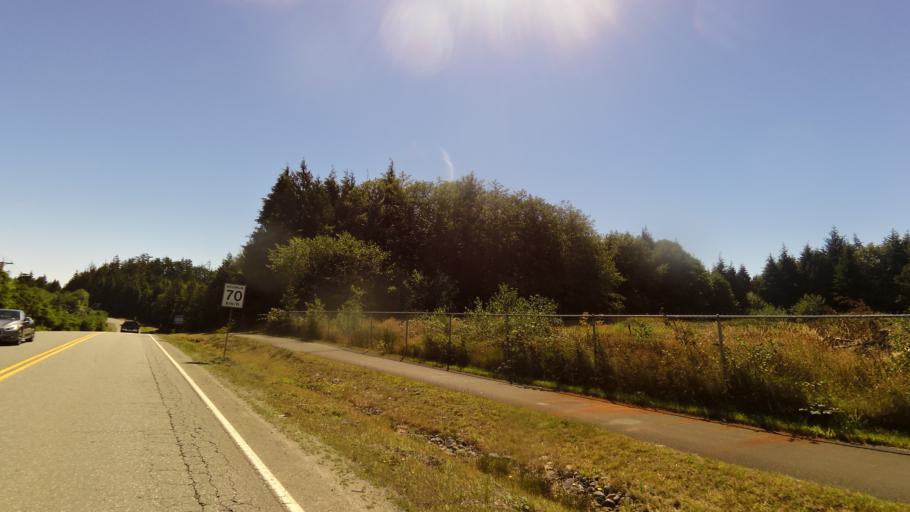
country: CA
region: British Columbia
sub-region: Regional District of Alberni-Clayoquot
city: Ucluelet
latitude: 48.9676
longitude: -125.5921
